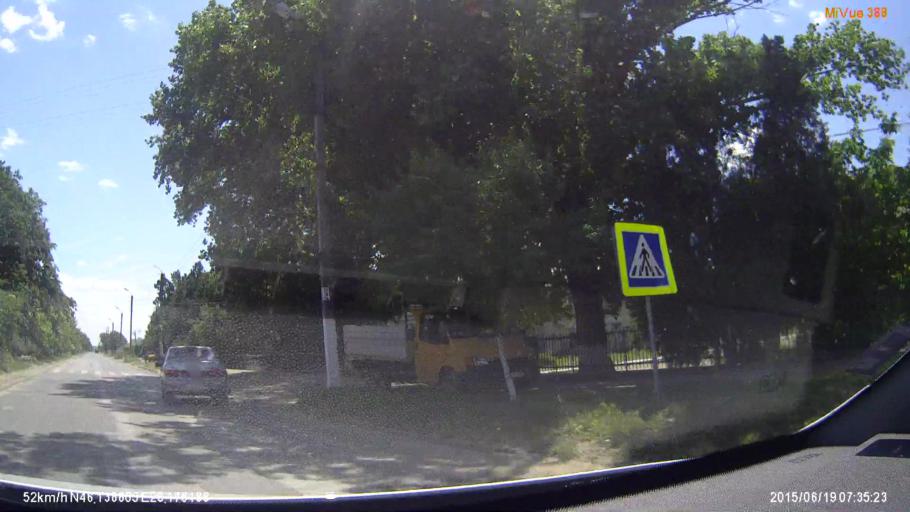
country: RO
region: Vaslui
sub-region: Oras Murgeni
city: Carja
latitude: 46.1392
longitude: 28.1750
